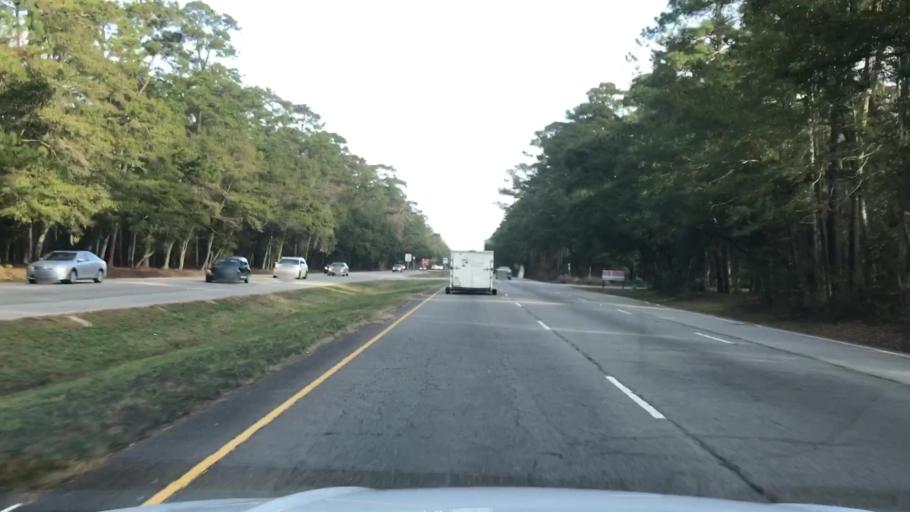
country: US
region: South Carolina
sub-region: Georgetown County
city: Murrells Inlet
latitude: 33.5132
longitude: -79.0737
